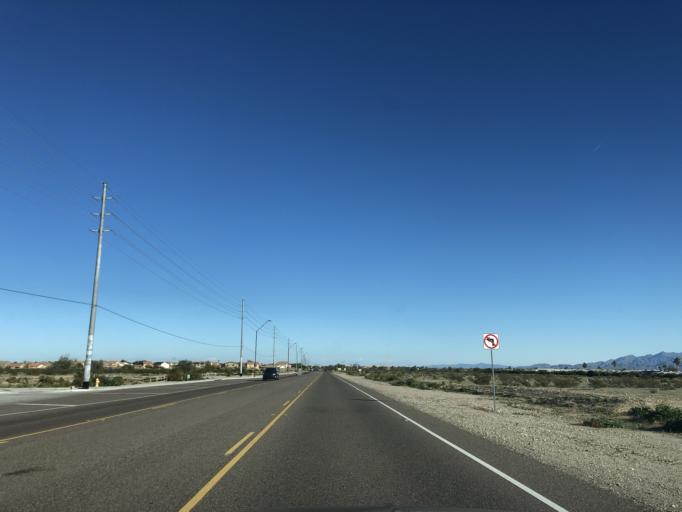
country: US
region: Arizona
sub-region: Maricopa County
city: Buckeye
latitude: 33.4354
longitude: -112.5792
